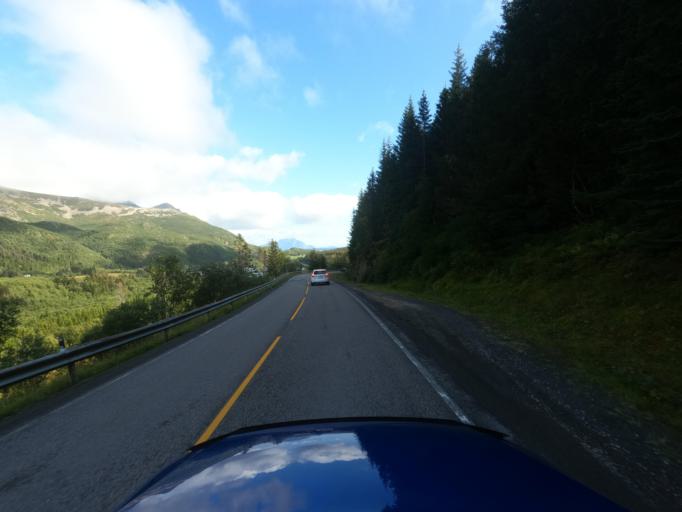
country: NO
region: Nordland
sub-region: Vestvagoy
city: Evjen
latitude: 68.1561
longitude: 13.7238
